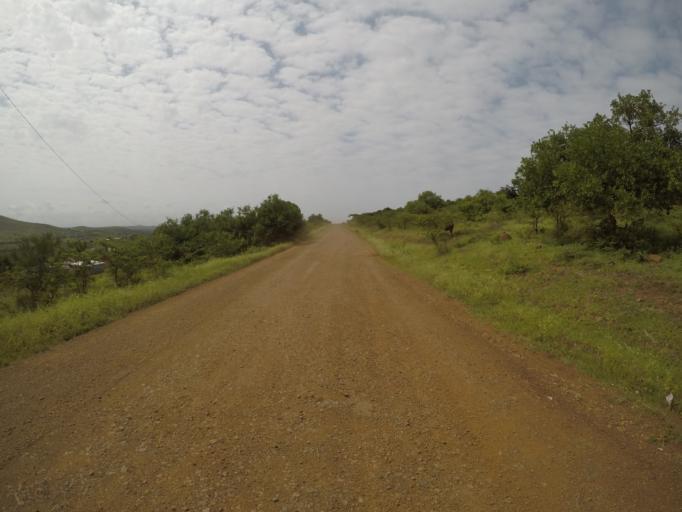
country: ZA
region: KwaZulu-Natal
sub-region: uThungulu District Municipality
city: Empangeni
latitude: -28.6213
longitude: 31.9052
